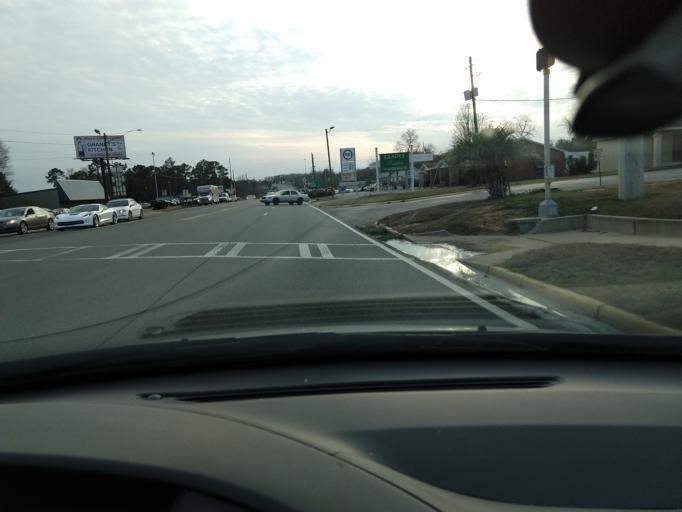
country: US
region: Georgia
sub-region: Sumter County
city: Americus
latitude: 32.0745
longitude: -84.2436
